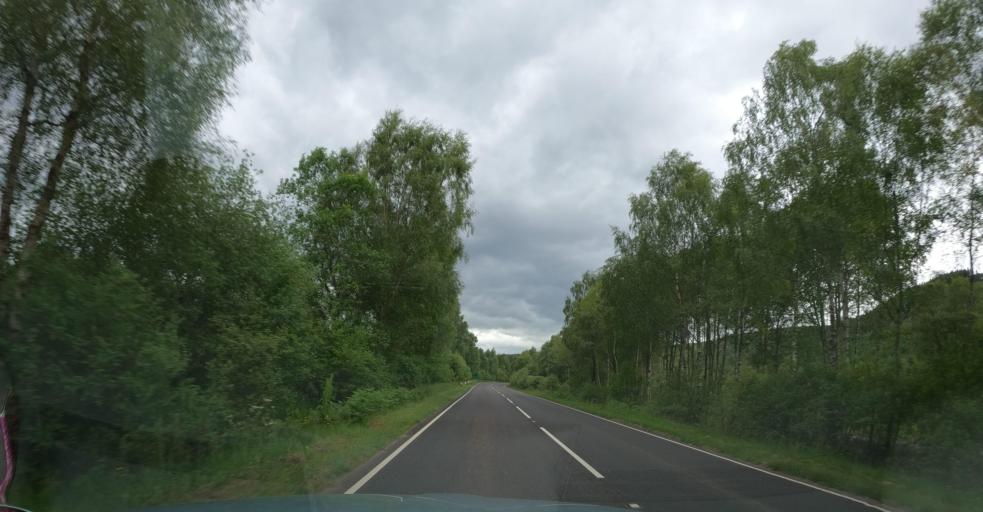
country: GB
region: Scotland
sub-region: Highland
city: Dingwall
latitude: 57.6652
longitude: -4.6683
